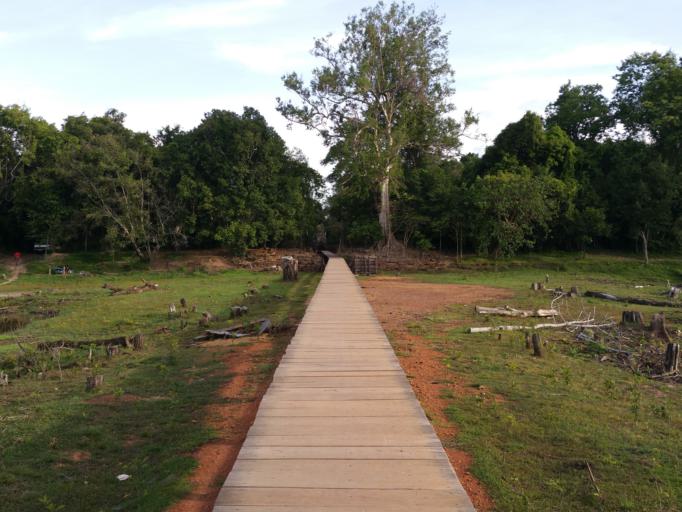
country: KH
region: Siem Reap
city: Siem Reap
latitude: 13.4654
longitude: 103.8948
